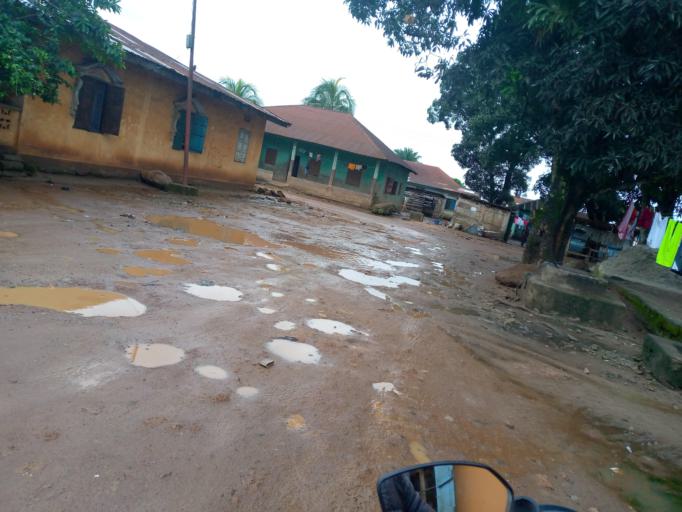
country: SL
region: Eastern Province
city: Kenema
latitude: 7.8850
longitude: -11.1841
